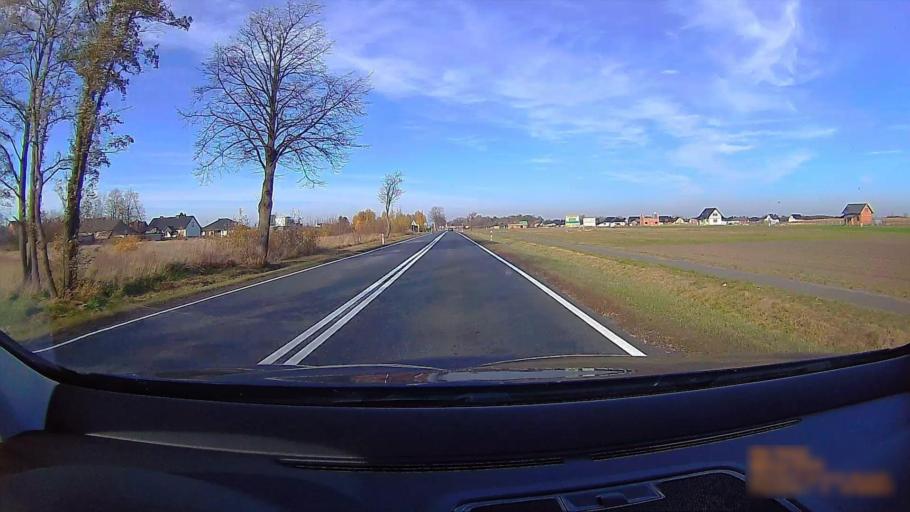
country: PL
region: Greater Poland Voivodeship
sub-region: Powiat koninski
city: Rychwal
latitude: 52.0586
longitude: 18.1636
